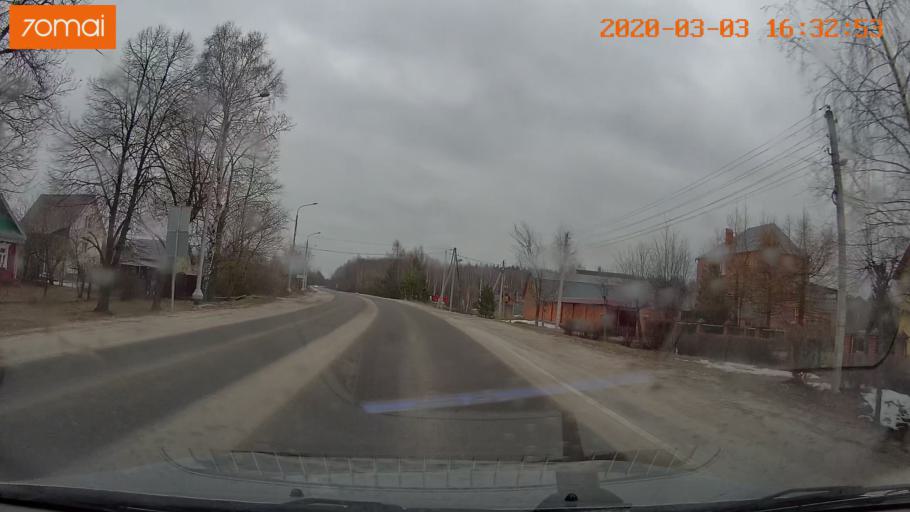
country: RU
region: Moskovskaya
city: Konobeyevo
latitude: 55.4184
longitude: 38.7364
